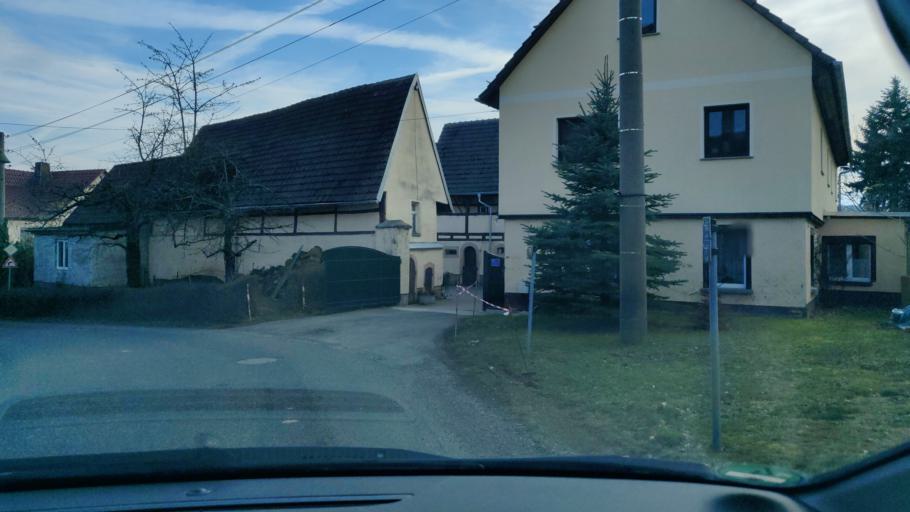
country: DE
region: Saxony
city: Konigsfeld
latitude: 51.0422
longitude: 12.7655
